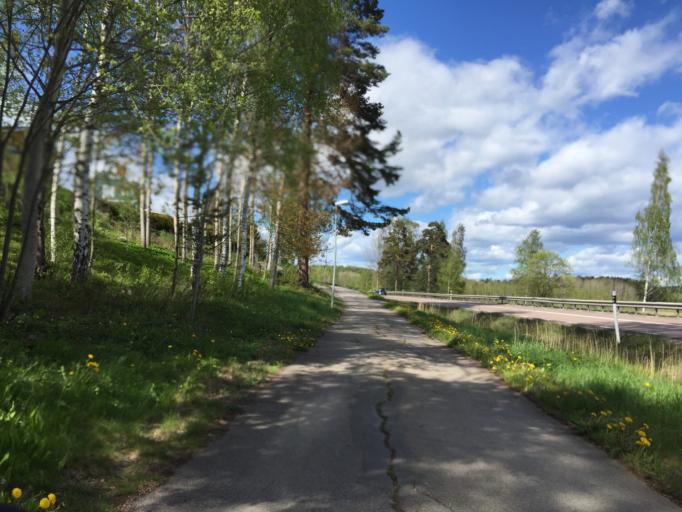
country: SE
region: Dalarna
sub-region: Ludvika Kommun
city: Ludvika
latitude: 60.1818
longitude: 15.2086
